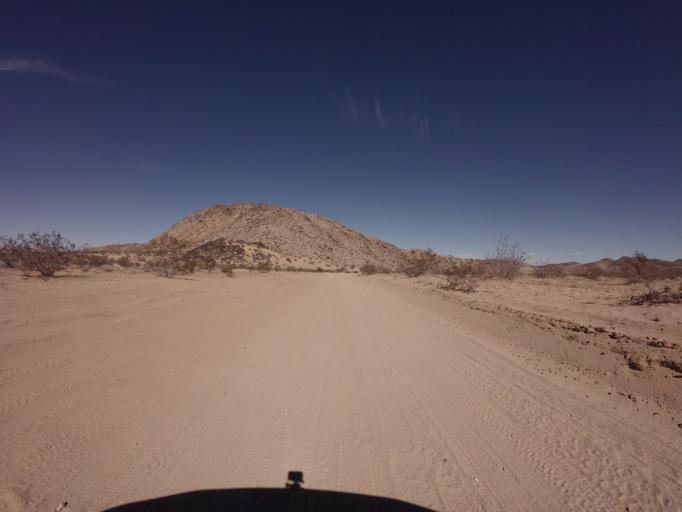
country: US
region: California
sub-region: San Bernardino County
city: Joshua Tree
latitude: 34.3136
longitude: -116.3969
